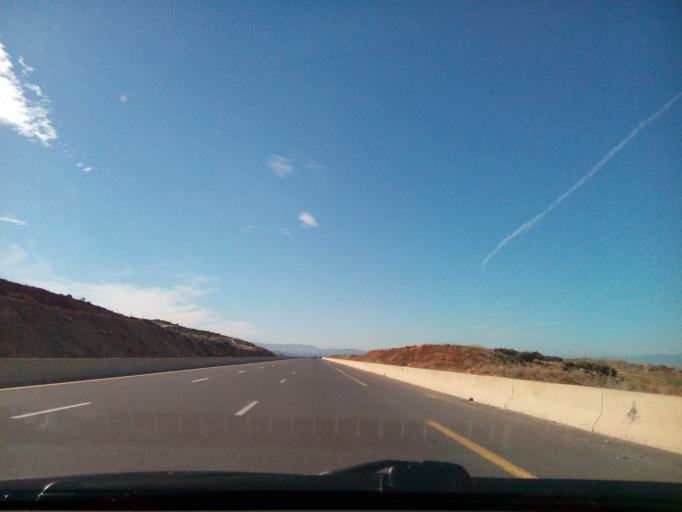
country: DZ
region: Tlemcen
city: Sidi Abdelli
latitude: 35.0155
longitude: -1.1523
